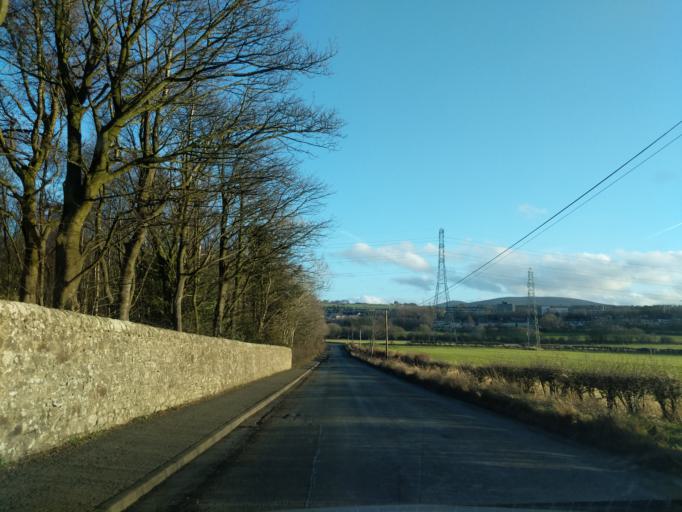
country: GB
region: Scotland
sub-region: Edinburgh
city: Currie
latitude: 55.9031
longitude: -3.3237
